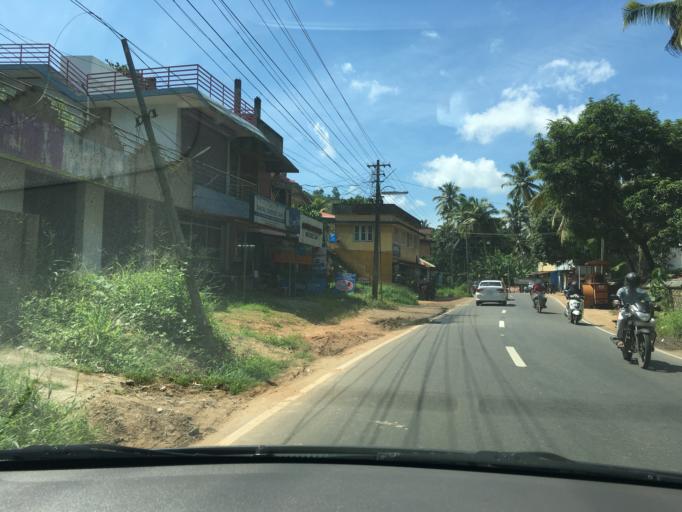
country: IN
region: Kerala
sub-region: Thiruvananthapuram
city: Nedumangad
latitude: 8.5699
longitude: 76.9892
